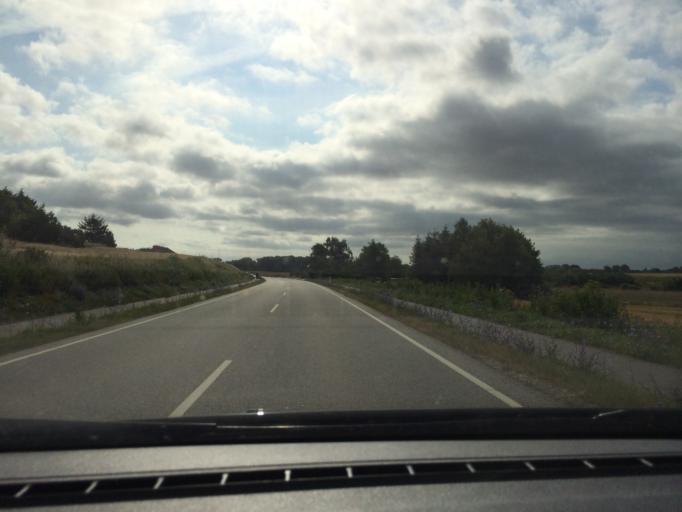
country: DK
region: Zealand
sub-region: Vordingborg Kommune
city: Stege
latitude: 54.9894
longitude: 12.3615
